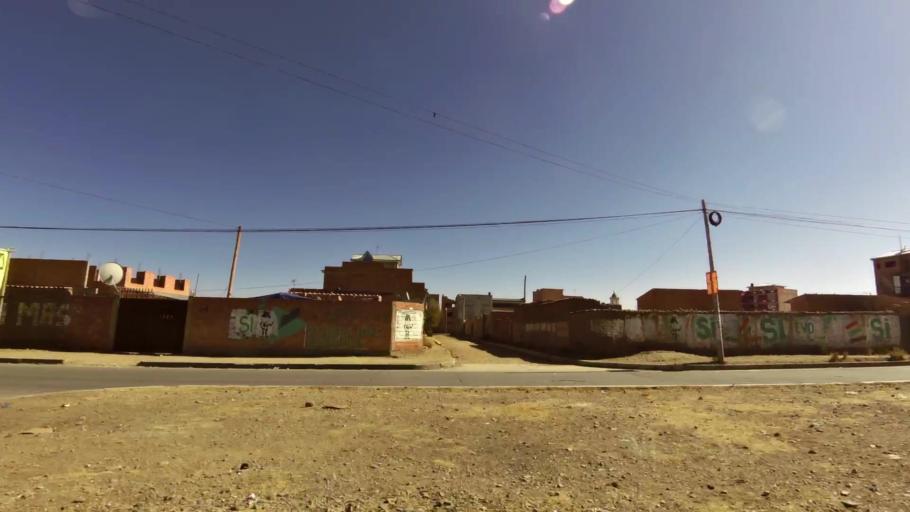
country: BO
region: La Paz
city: La Paz
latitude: -16.5294
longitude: -68.2084
